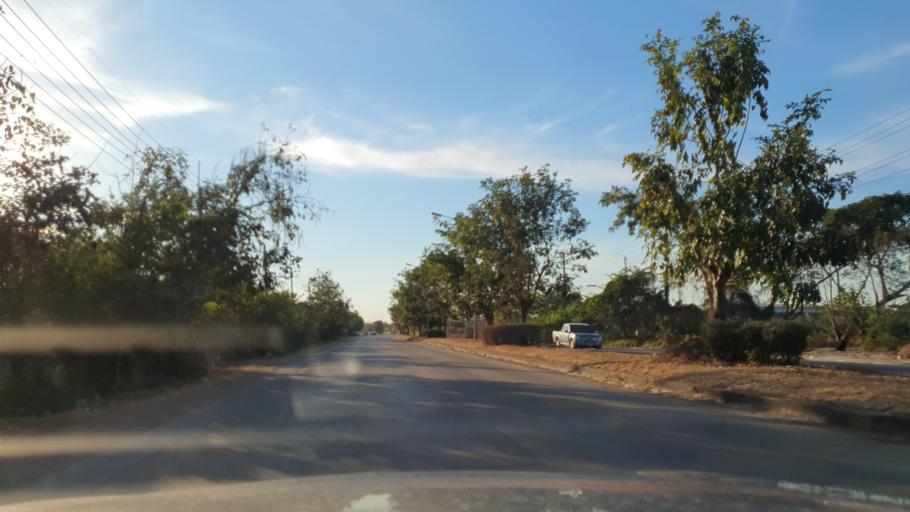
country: TH
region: Khon Kaen
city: Khon Kaen
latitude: 16.4374
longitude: 102.9063
